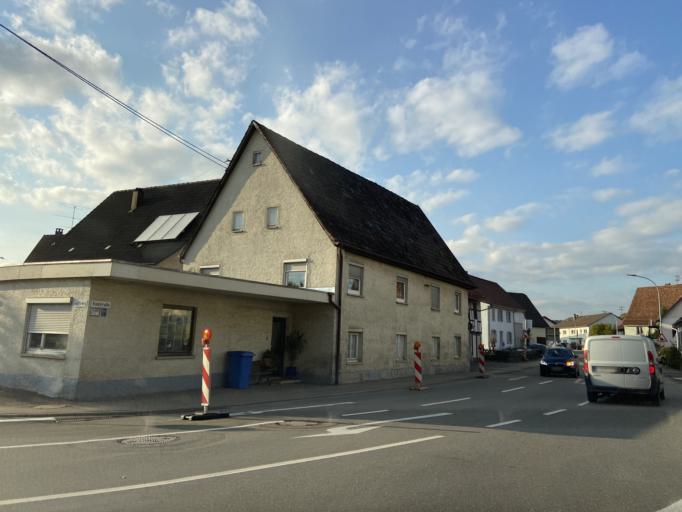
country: DE
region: Baden-Wuerttemberg
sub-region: Tuebingen Region
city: Bingen
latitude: 48.1049
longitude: 9.2894
